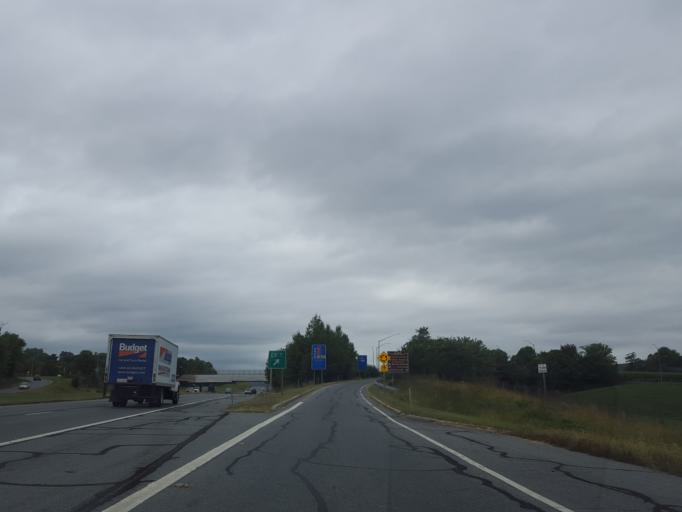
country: US
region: Maryland
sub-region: Frederick County
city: Brunswick
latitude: 39.3415
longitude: -77.6380
